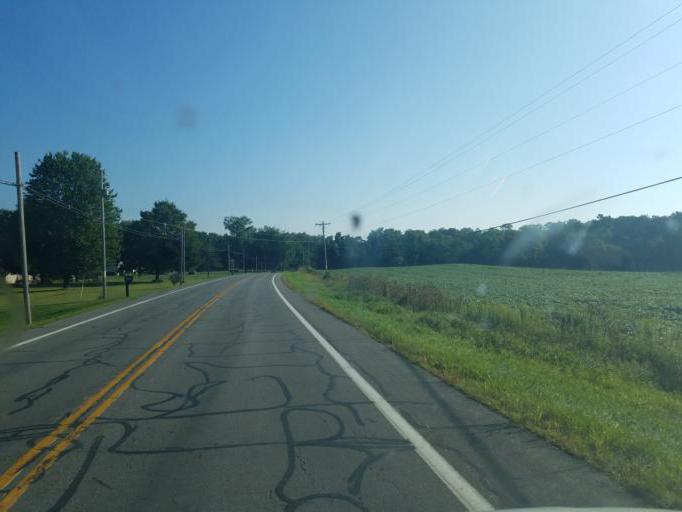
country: US
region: Ohio
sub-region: Richland County
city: Lexington
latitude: 40.6511
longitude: -82.6207
